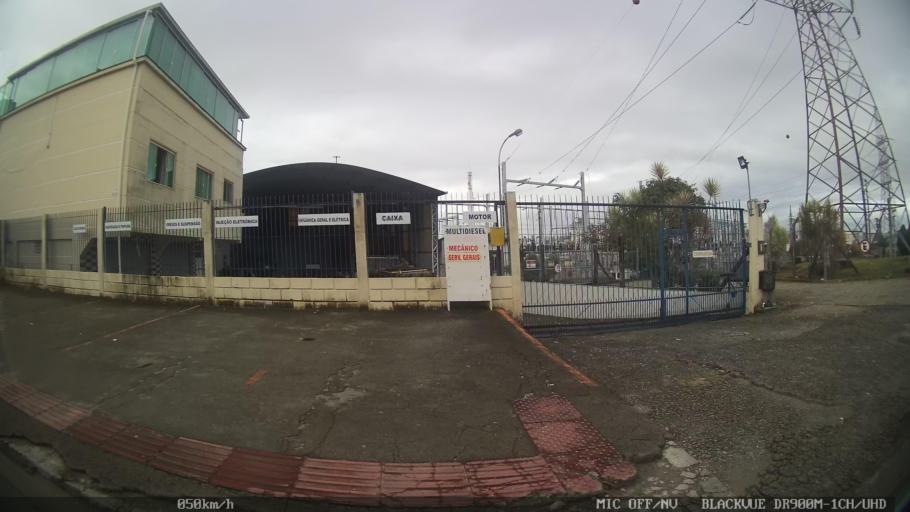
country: BR
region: Santa Catarina
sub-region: Sao Jose
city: Campinas
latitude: -27.5860
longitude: -48.6195
